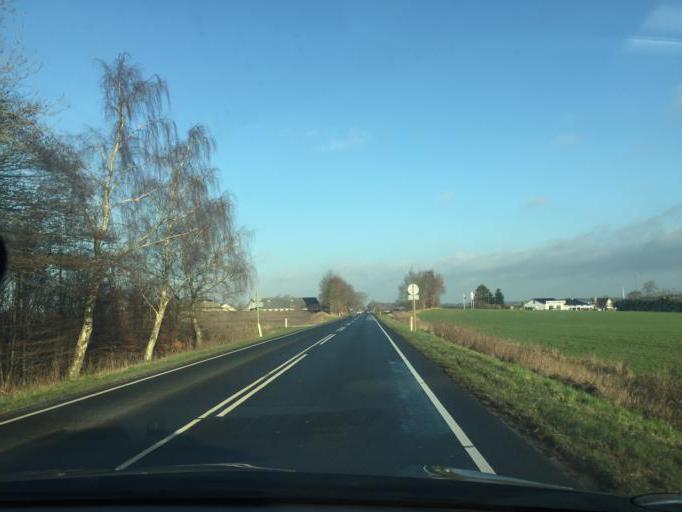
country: DK
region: South Denmark
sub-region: Faaborg-Midtfyn Kommune
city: Faaborg
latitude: 55.1805
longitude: 10.2981
